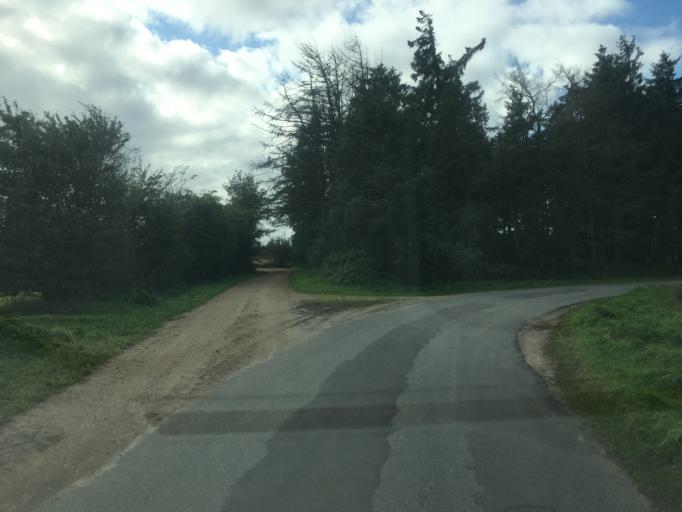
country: DK
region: South Denmark
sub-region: Tonder Kommune
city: Logumkloster
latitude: 55.1083
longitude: 8.8813
